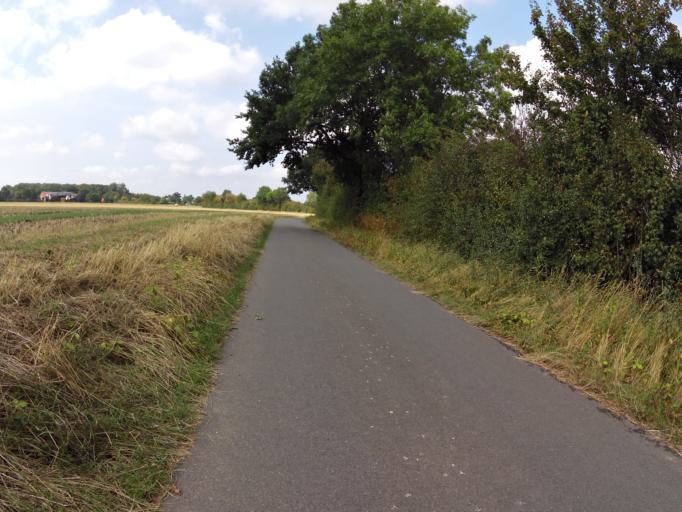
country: DE
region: Lower Saxony
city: Bucken
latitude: 52.7780
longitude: 9.1561
